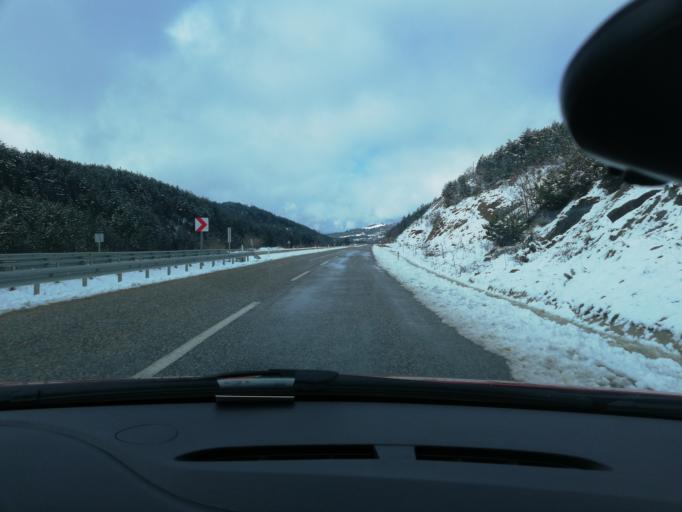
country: TR
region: Kastamonu
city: Akkaya
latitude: 41.2808
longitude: 33.4273
